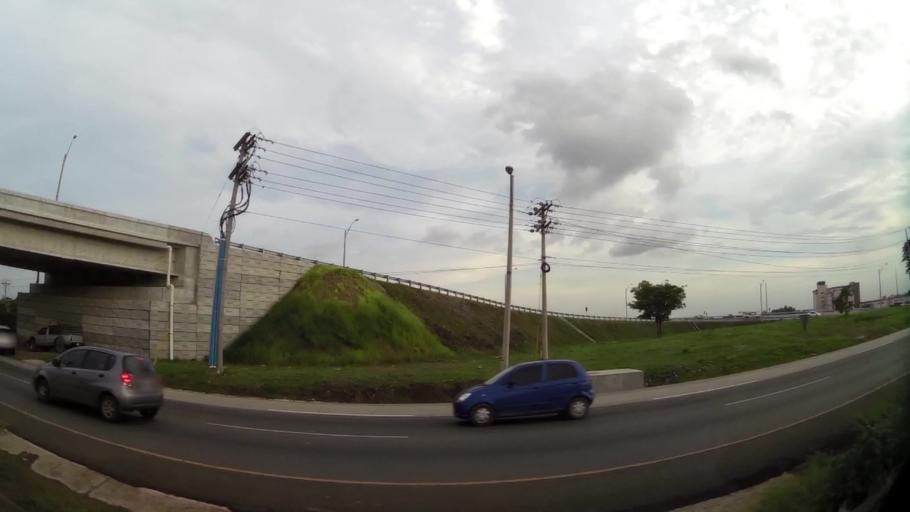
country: PA
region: Panama
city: Tocumen
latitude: 9.0983
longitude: -79.3915
